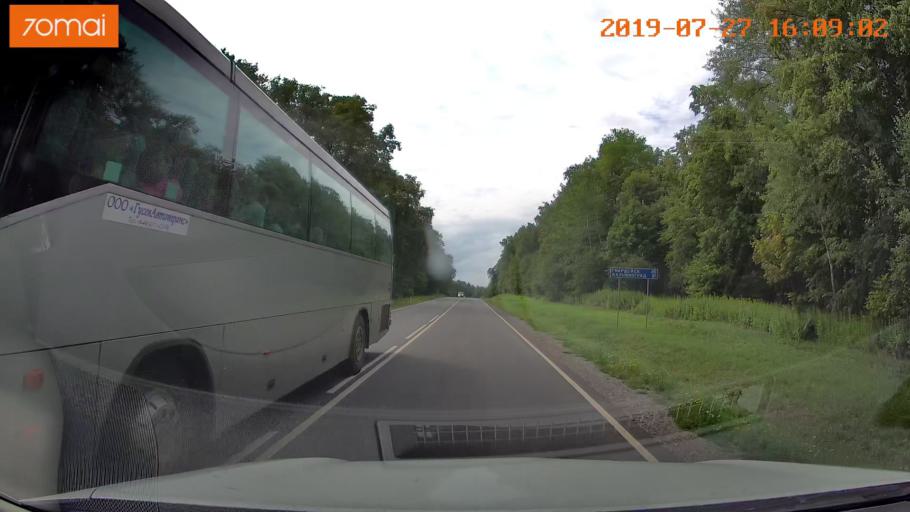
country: RU
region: Kaliningrad
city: Chernyakhovsk
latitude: 54.6384
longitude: 21.7234
